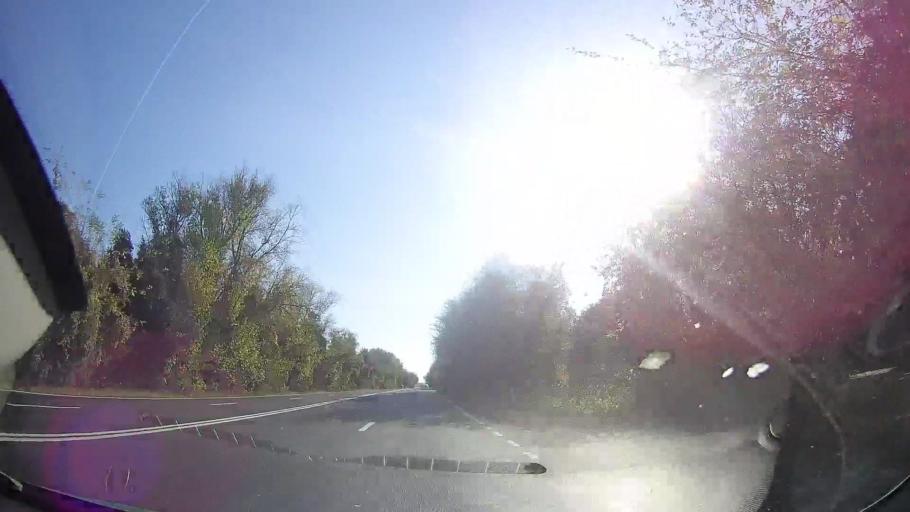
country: RO
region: Constanta
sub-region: Comuna Douazeci si Trei August
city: Dulcesti
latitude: 43.8659
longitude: 28.5750
